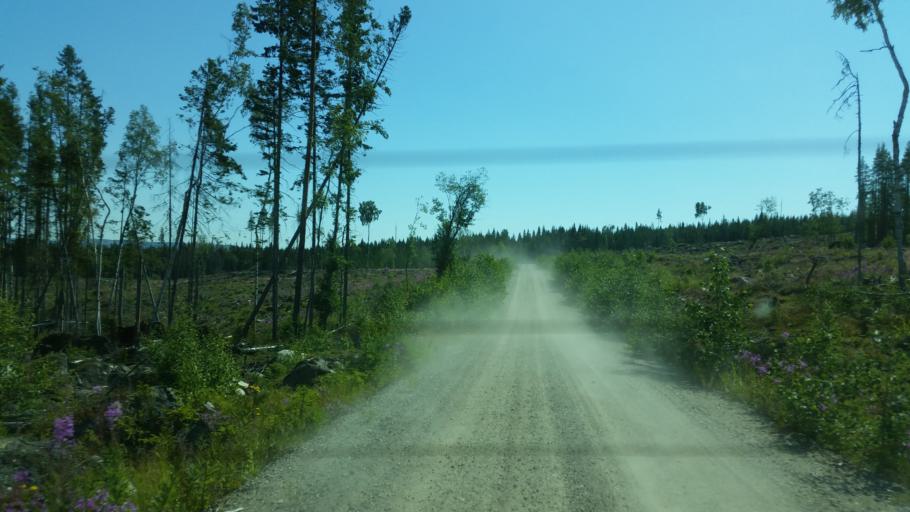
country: SE
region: Vaesternorrland
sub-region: Ange Kommun
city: Ange
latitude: 62.2015
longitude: 15.4768
